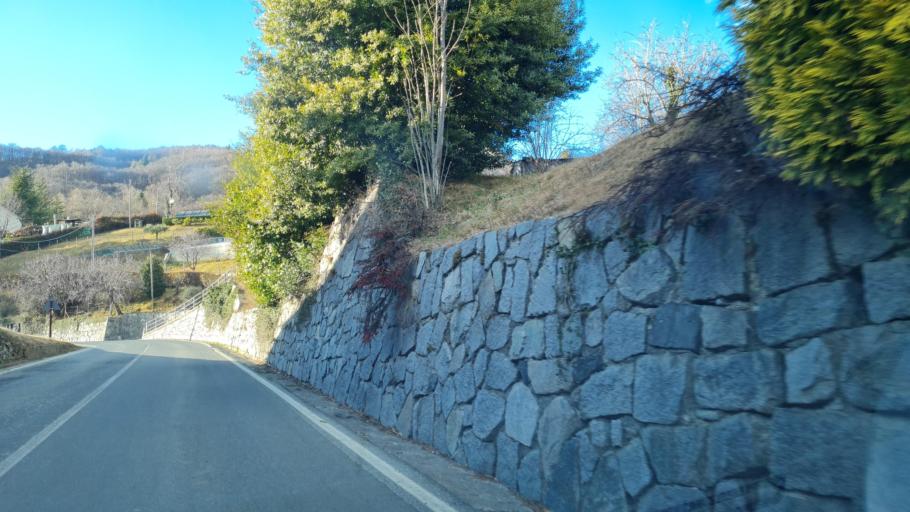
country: IT
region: Piedmont
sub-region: Provincia di Biella
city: Sordevolo
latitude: 45.5789
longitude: 7.9871
